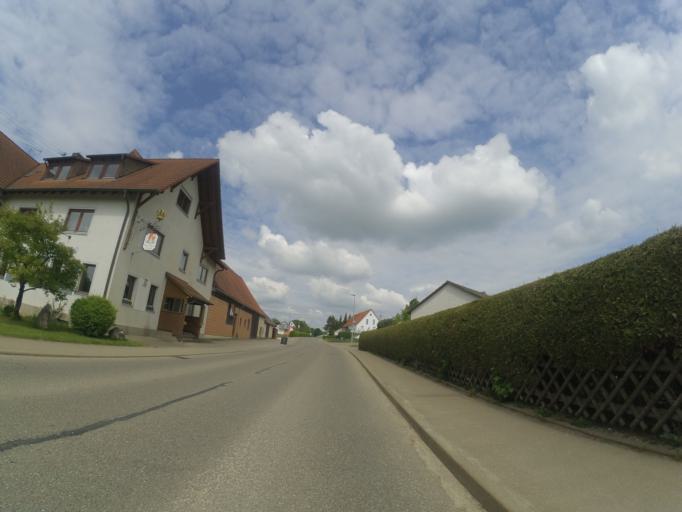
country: DE
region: Baden-Wuerttemberg
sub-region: Tuebingen Region
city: Berghulen
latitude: 48.4585
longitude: 9.7773
